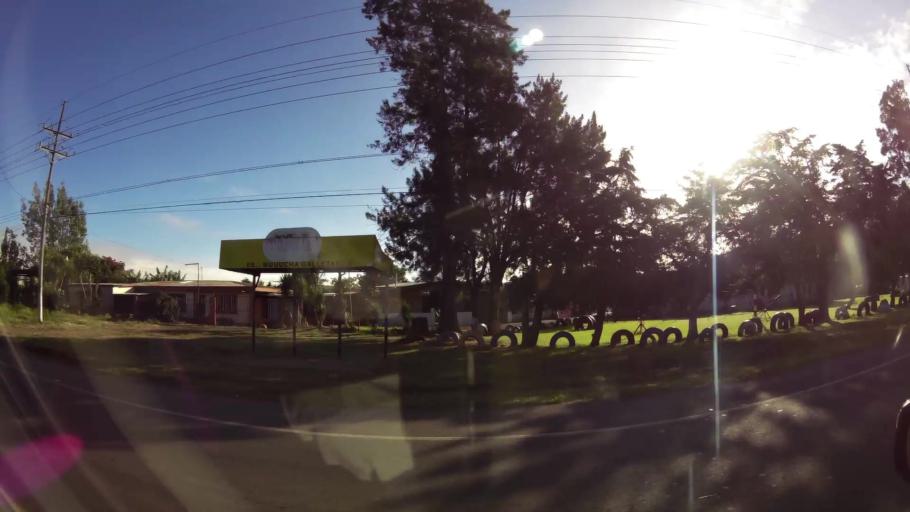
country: CR
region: Cartago
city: Tobosi
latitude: 9.8366
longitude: -83.9511
